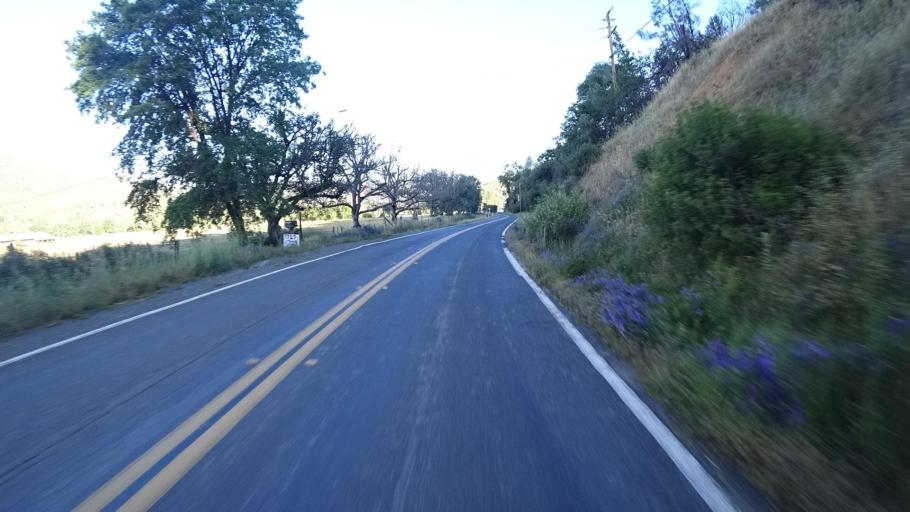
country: US
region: California
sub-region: Lake County
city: Upper Lake
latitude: 39.2018
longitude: -122.9030
